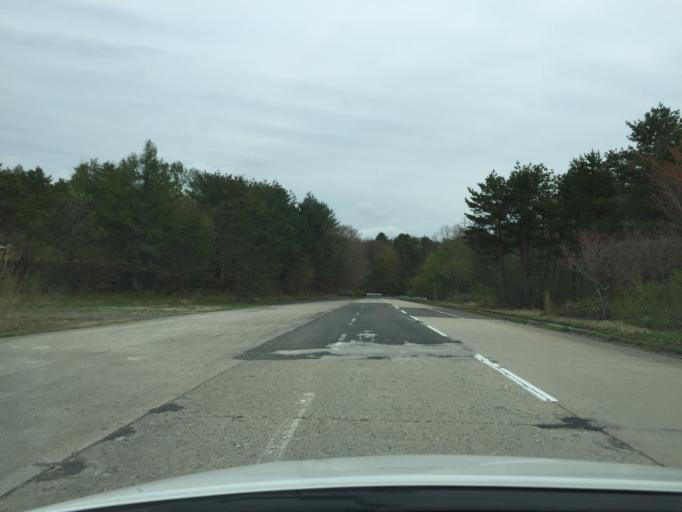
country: JP
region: Fukushima
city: Inawashiro
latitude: 37.6120
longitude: 140.2288
